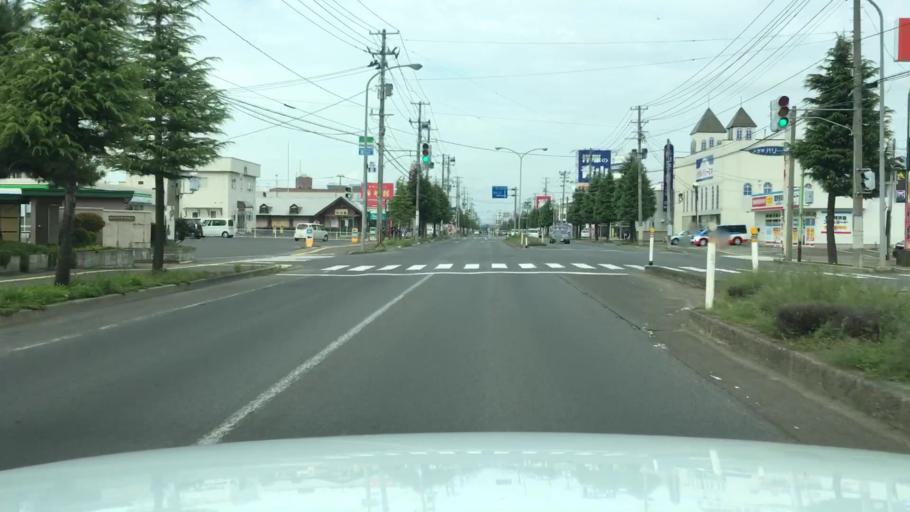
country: JP
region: Aomori
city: Hirosaki
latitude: 40.6132
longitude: 140.4831
